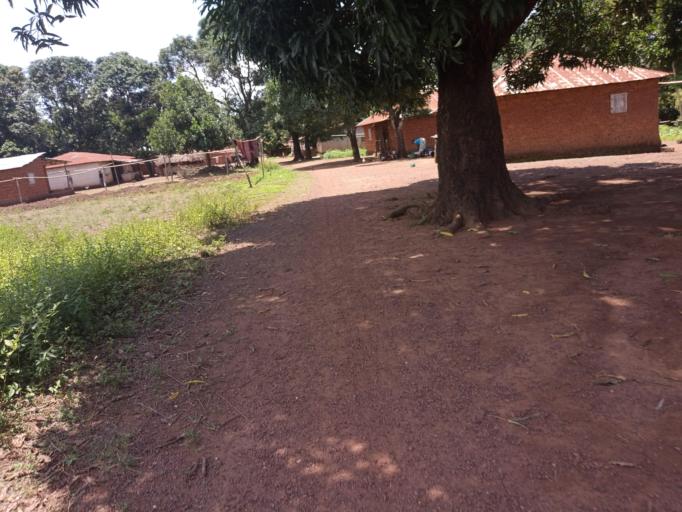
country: SL
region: Northern Province
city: Kamakwie
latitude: 9.4683
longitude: -12.2489
